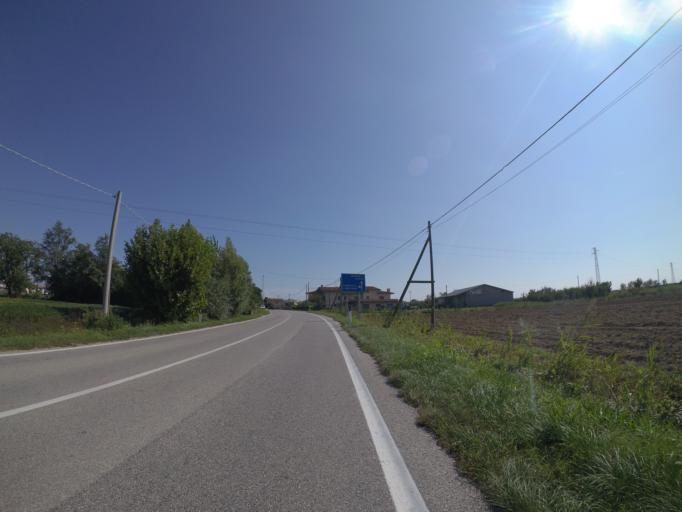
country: IT
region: Friuli Venezia Giulia
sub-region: Provincia di Udine
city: Marano Lagunare
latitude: 45.7750
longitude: 13.1645
